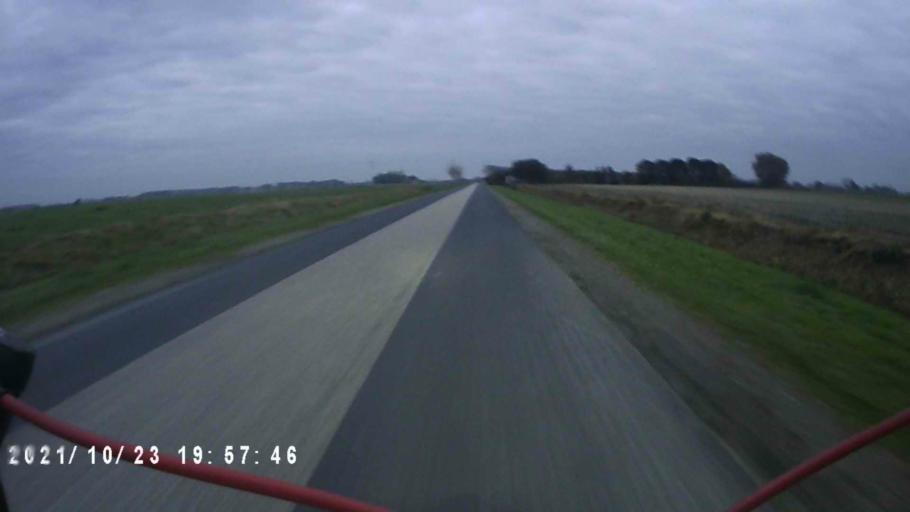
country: NL
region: Friesland
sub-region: Gemeente Harlingen
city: Harlingen
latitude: 53.1138
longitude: 5.4481
